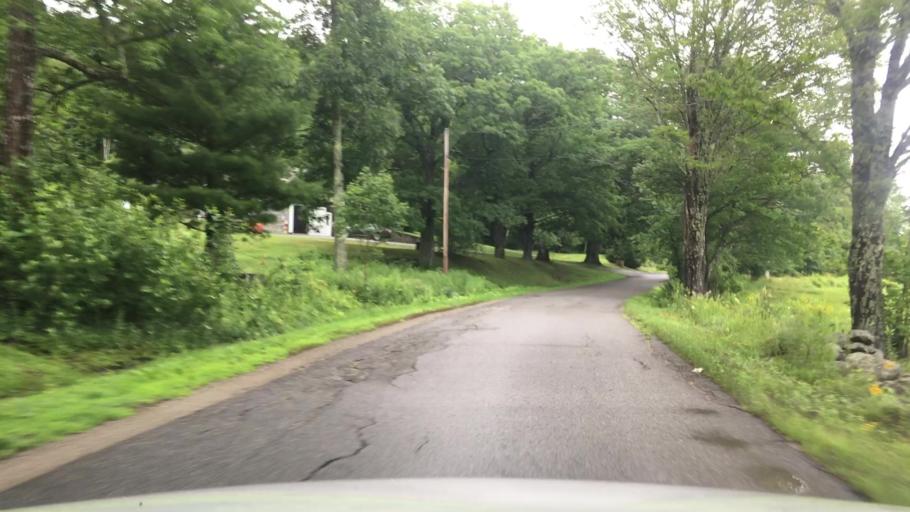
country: US
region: Maine
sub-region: Knox County
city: Hope
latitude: 44.2303
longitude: -69.1770
